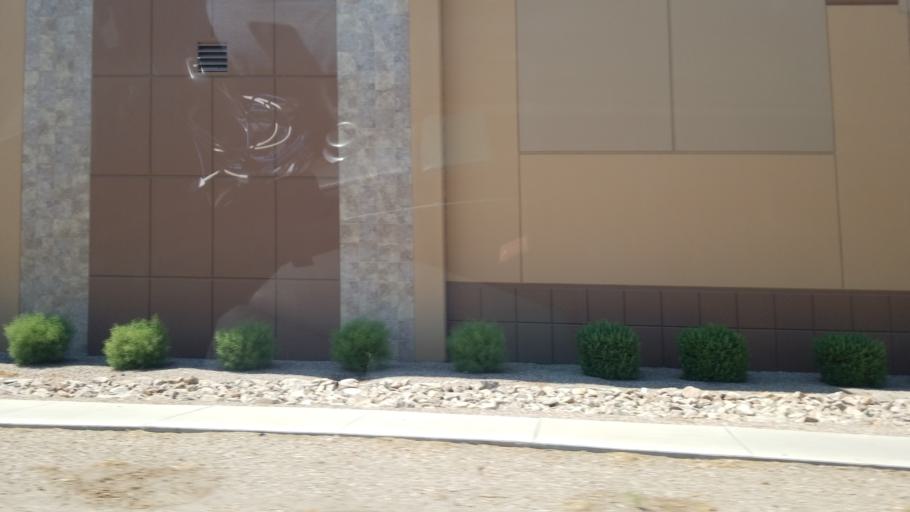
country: US
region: Arizona
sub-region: Maricopa County
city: Phoenix
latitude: 33.4368
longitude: -112.1463
